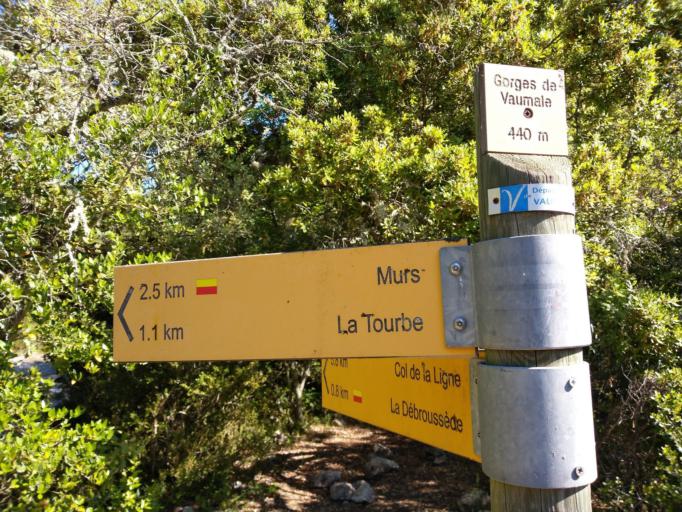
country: FR
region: Provence-Alpes-Cote d'Azur
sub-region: Departement du Vaucluse
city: Roussillon
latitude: 43.9617
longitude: 5.2648
